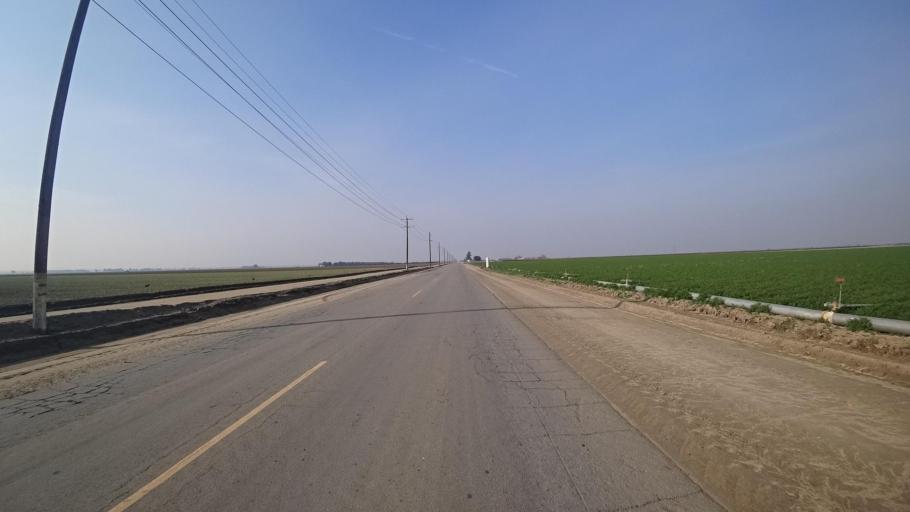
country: US
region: California
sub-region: Kern County
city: Arvin
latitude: 35.0928
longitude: -118.8538
